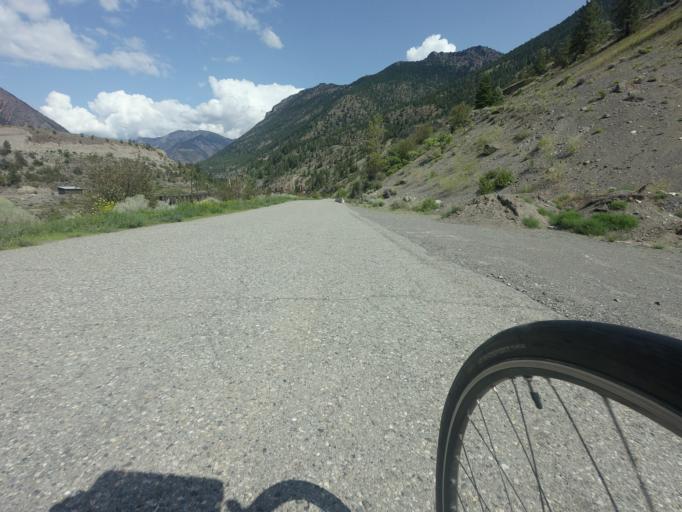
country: CA
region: British Columbia
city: Lillooet
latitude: 50.7089
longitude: -121.9108
